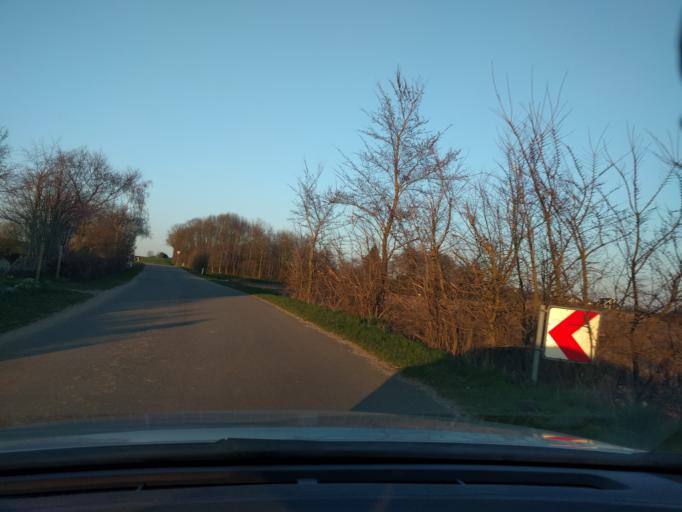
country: DK
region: South Denmark
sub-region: Assens Kommune
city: Glamsbjerg
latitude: 55.2626
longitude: 10.0156
